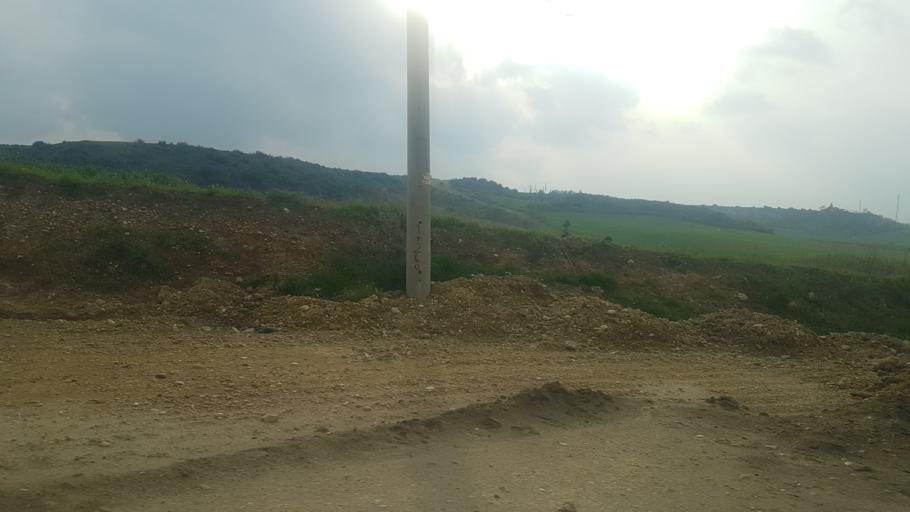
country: TR
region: Adana
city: Seyhan
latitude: 37.0429
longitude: 35.2131
